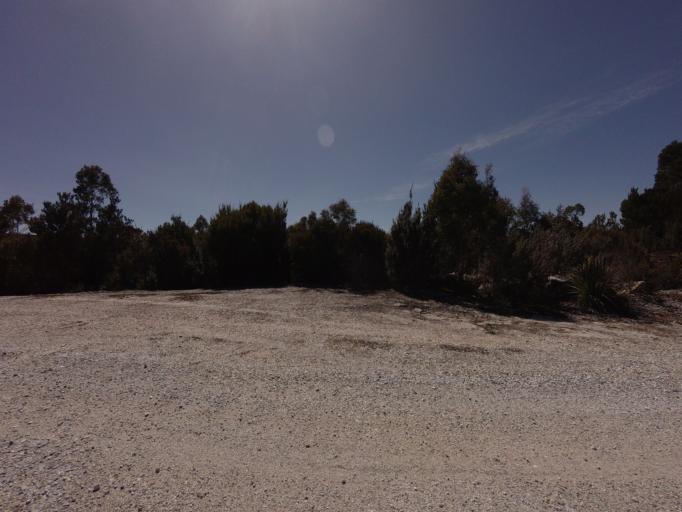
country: AU
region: Tasmania
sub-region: Huon Valley
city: Geeveston
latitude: -43.0336
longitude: 146.2951
